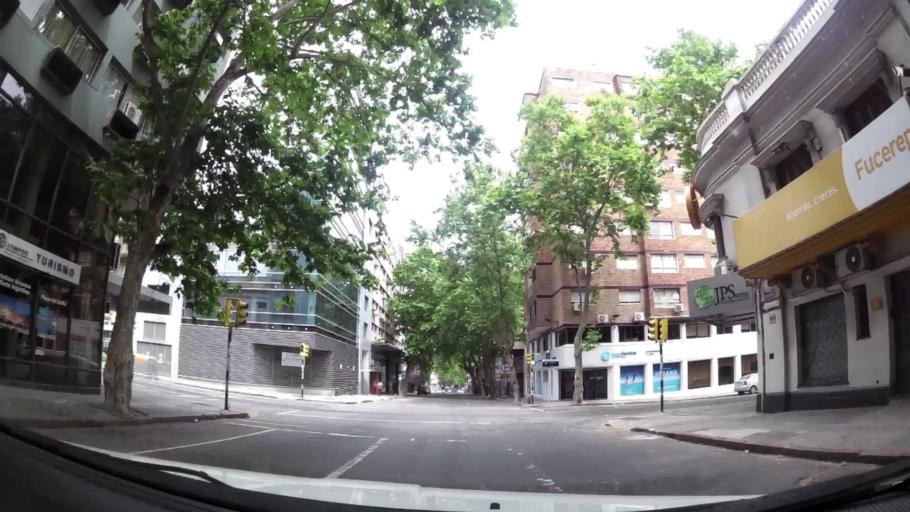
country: UY
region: Montevideo
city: Montevideo
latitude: -34.9052
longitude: -56.1959
